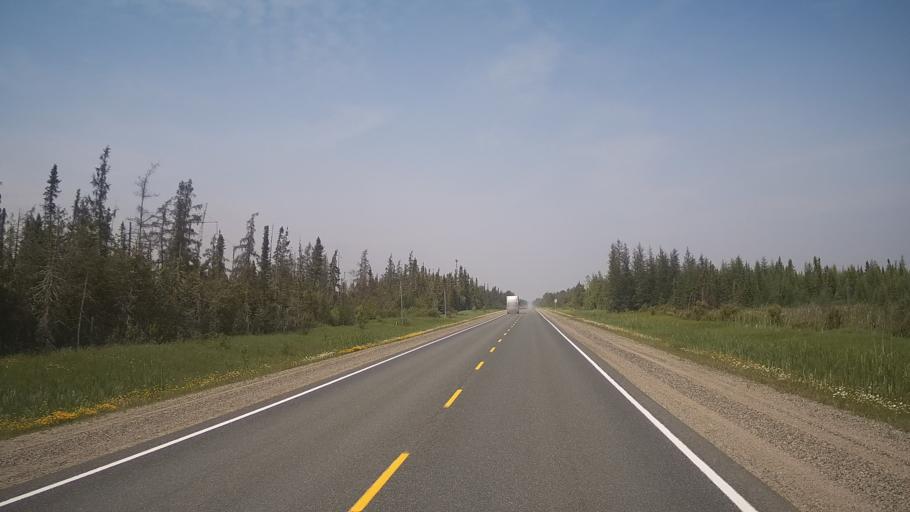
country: CA
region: Ontario
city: Timmins
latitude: 48.7917
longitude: -81.3660
